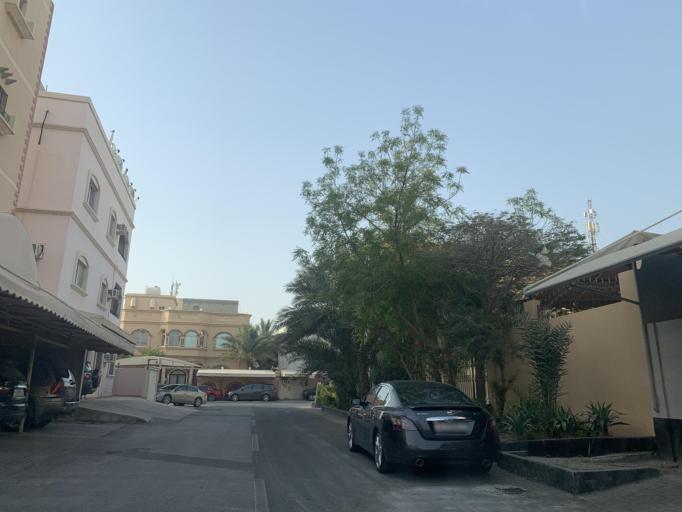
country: BH
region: Northern
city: Madinat `Isa
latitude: 26.1942
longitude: 50.5620
